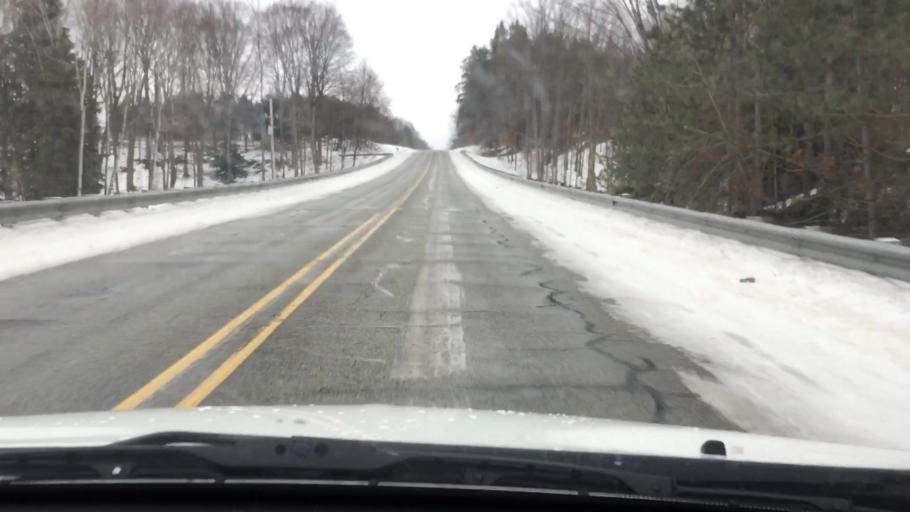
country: US
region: Michigan
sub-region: Wexford County
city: Cadillac
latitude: 44.1772
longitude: -85.4055
